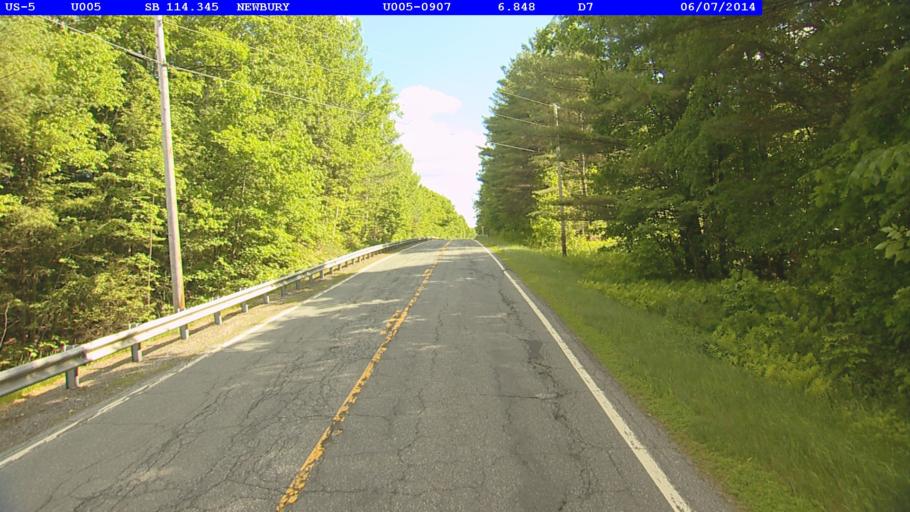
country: US
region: New Hampshire
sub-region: Grafton County
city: Woodsville
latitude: 44.1188
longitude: -72.0541
